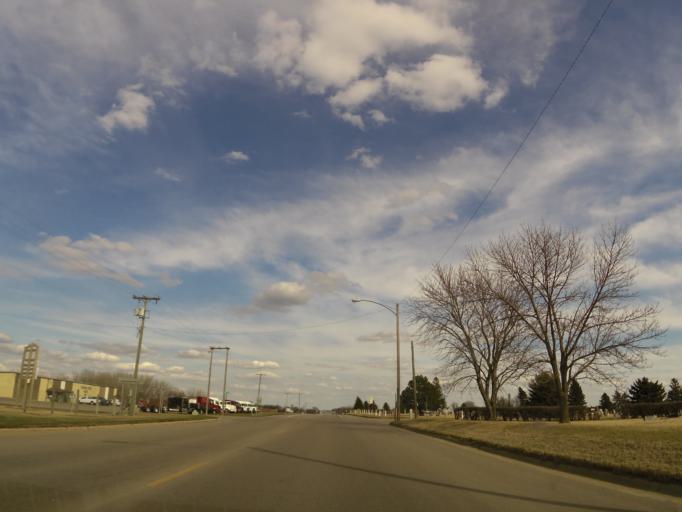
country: US
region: Minnesota
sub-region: Lac qui Parle County
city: Dawson
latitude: 44.9358
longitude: -96.0438
